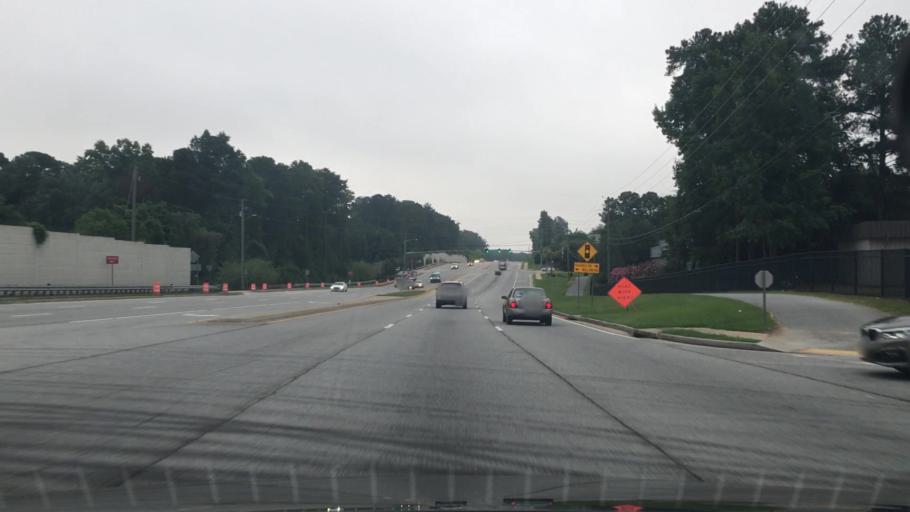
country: US
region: Georgia
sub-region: Fayette County
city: Peachtree City
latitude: 33.3936
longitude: -84.5864
